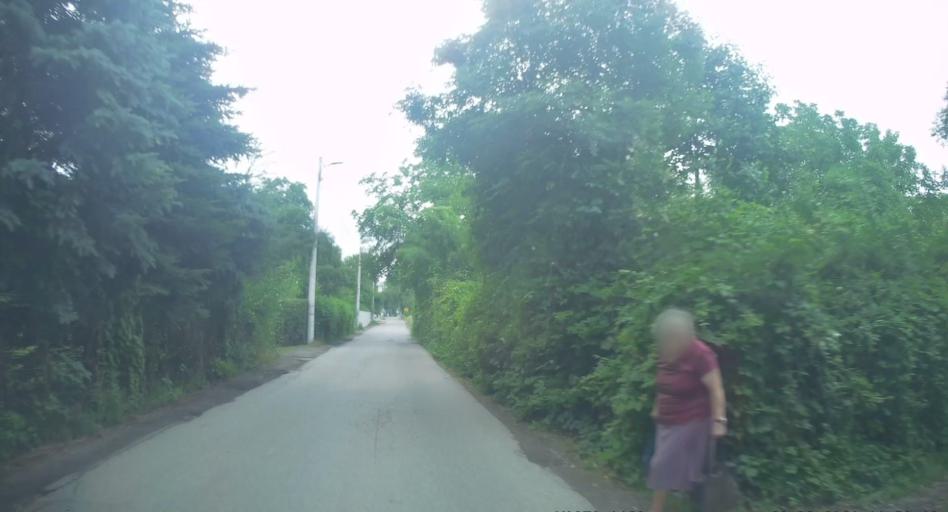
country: PL
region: Lesser Poland Voivodeship
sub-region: Krakow
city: Krakow
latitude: 50.0641
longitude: 19.8997
